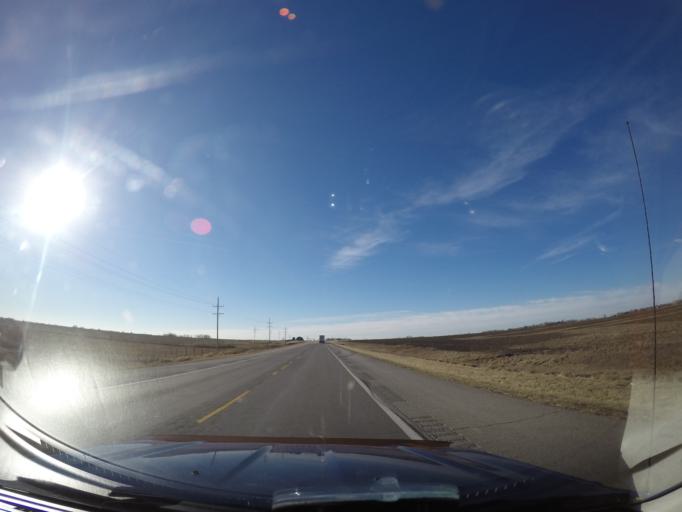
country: US
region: Kansas
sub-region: Marion County
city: Hillsboro
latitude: 38.3623
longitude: -97.3008
